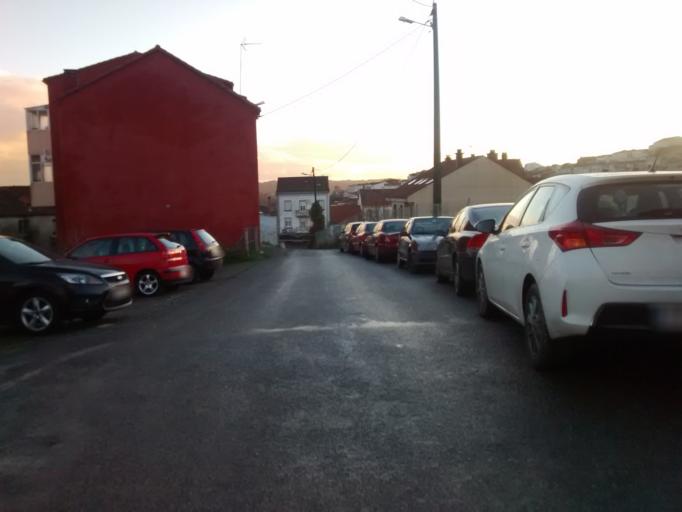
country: ES
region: Galicia
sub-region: Provincia da Coruna
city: Santiago de Compostela
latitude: 42.8859
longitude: -8.5316
